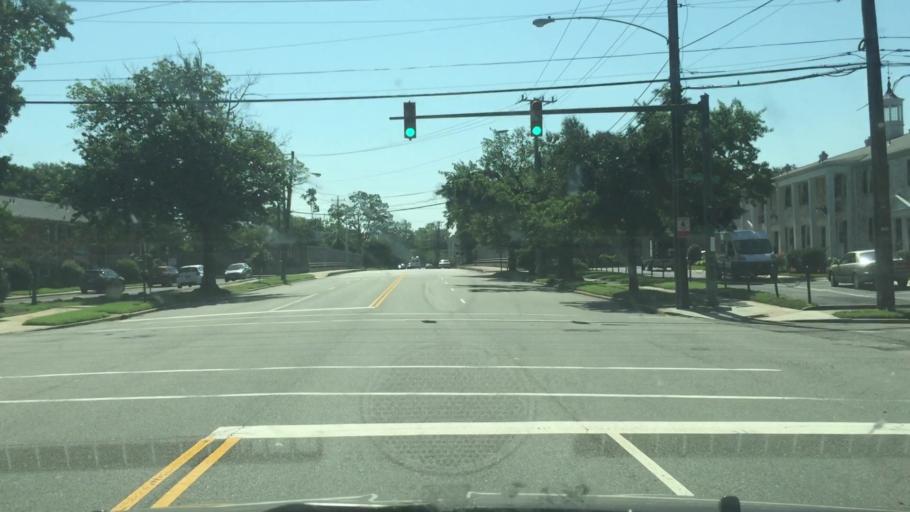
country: US
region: Virginia
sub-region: City of Richmond
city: Richmond
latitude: 37.5642
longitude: -77.4859
